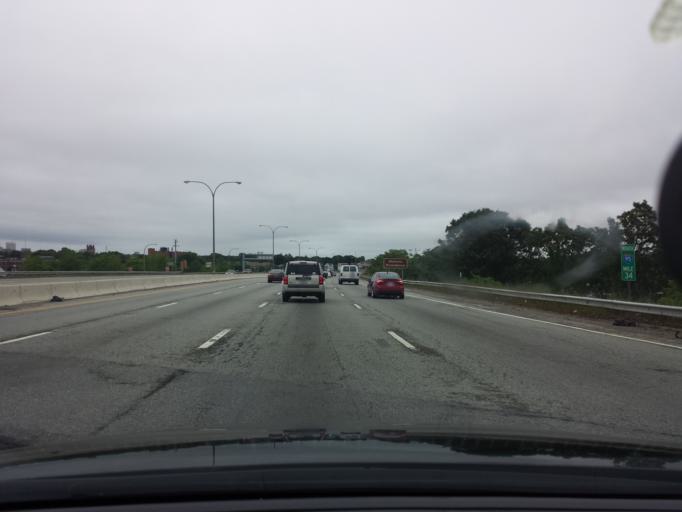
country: US
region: Rhode Island
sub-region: Providence County
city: Cranston
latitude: 41.7877
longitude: -71.4202
